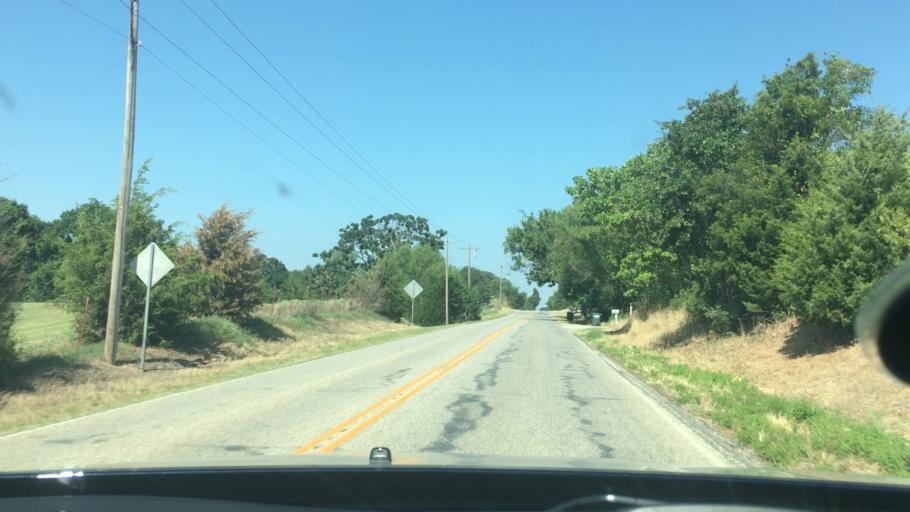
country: US
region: Oklahoma
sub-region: Johnston County
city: Tishomingo
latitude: 34.2377
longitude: -96.5637
